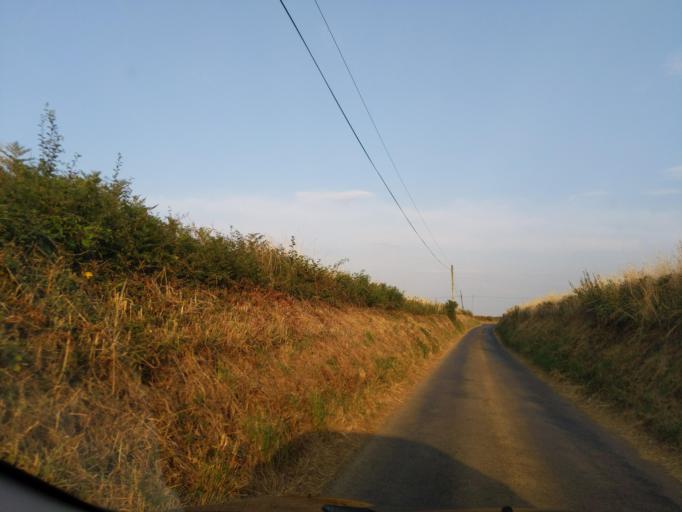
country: GB
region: England
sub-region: Cornwall
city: Fowey
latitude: 50.3674
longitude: -4.5860
